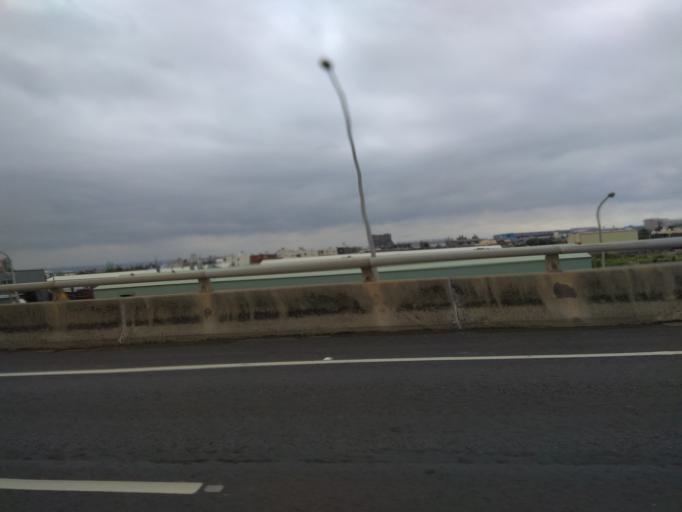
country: TW
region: Taiwan
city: Taoyuan City
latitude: 25.0859
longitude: 121.1840
